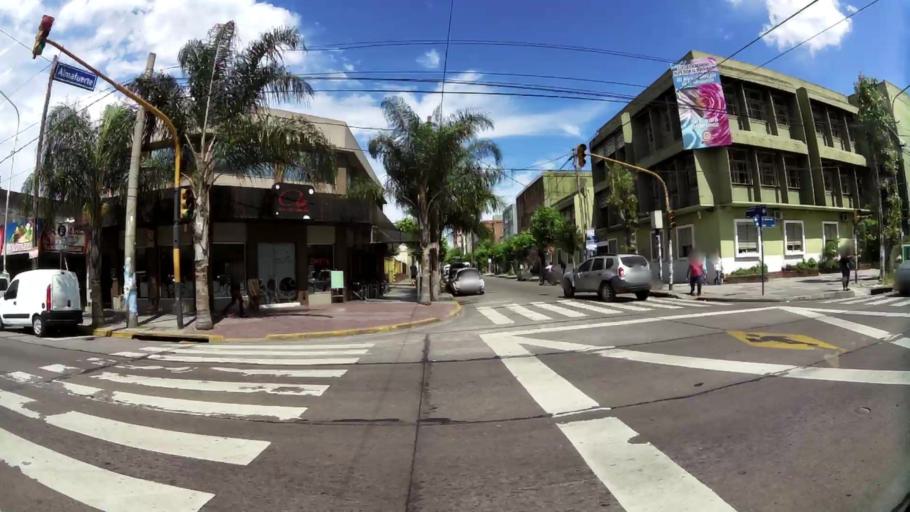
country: AR
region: Buenos Aires
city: San Justo
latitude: -34.6752
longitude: -58.5634
